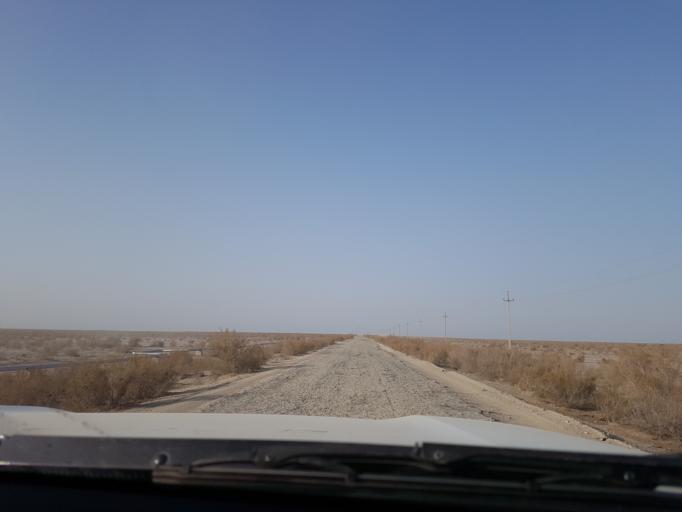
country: UZ
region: Karakalpakstan
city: Shumanay Shahri
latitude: 42.0114
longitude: 58.0983
